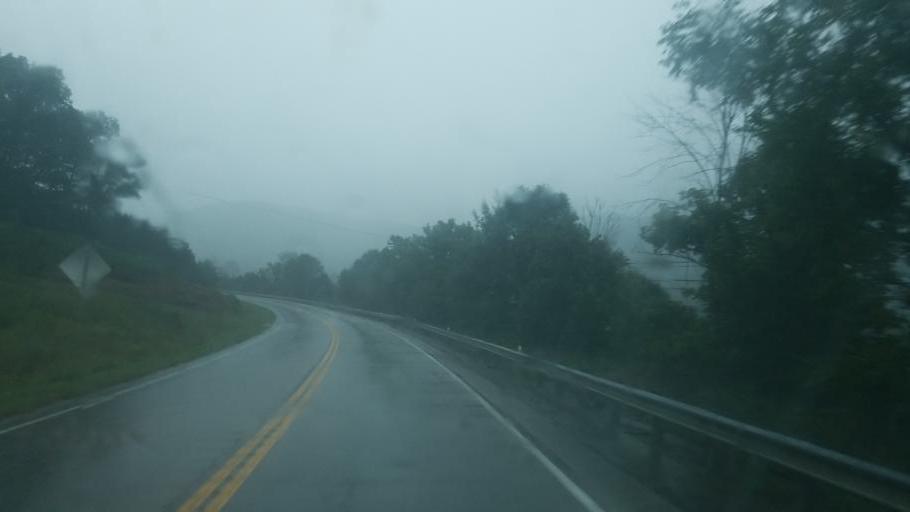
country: US
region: Kentucky
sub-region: Rowan County
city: Morehead
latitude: 38.2865
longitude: -83.5705
